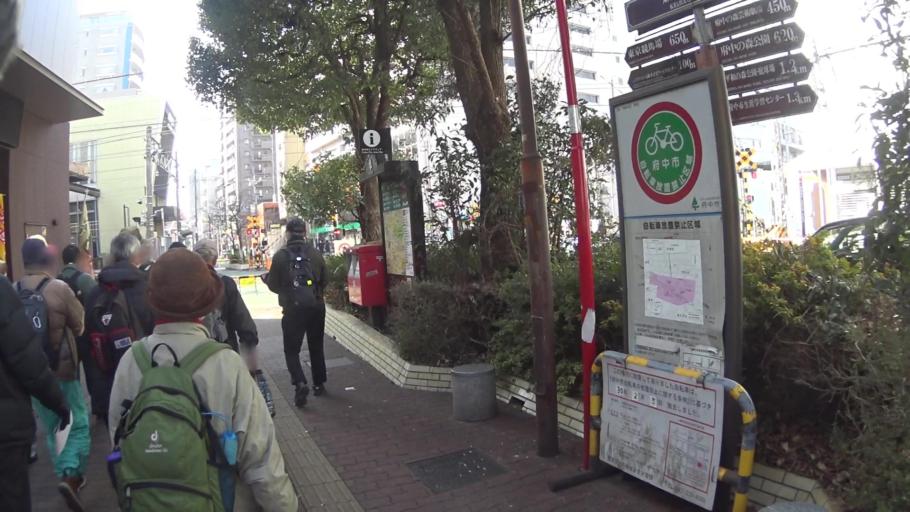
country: JP
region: Tokyo
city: Kokubunji
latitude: 35.6714
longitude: 139.4941
